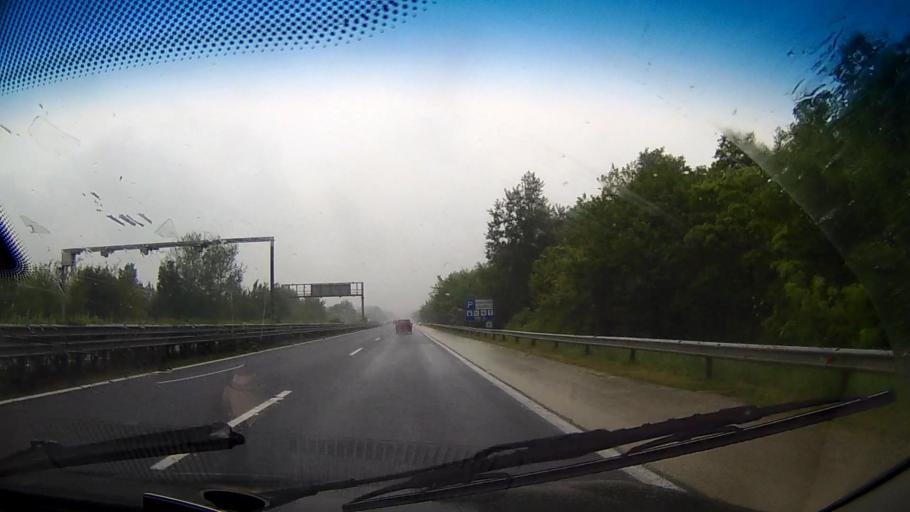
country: HU
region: Komarom-Esztergom
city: Vertesszolos
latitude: 47.6126
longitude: 18.3543
